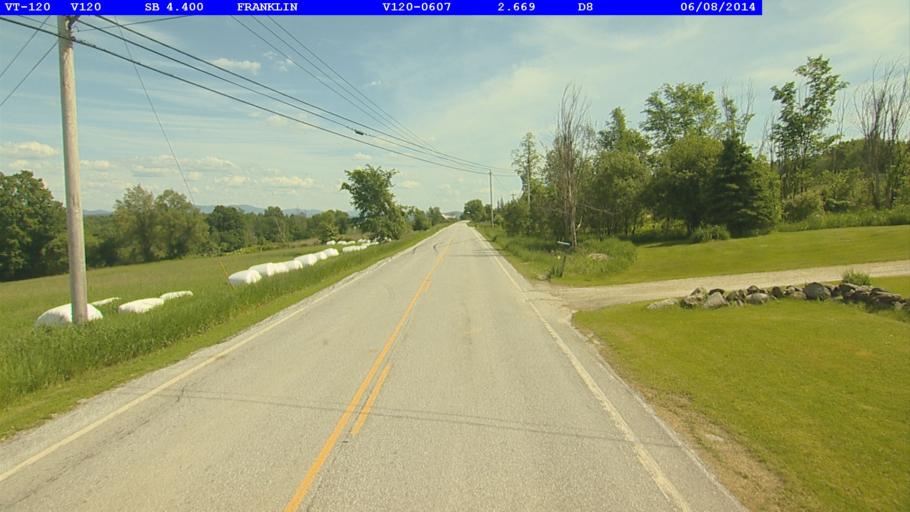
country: US
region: Vermont
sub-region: Franklin County
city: Enosburg Falls
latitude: 44.9712
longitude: -72.9101
